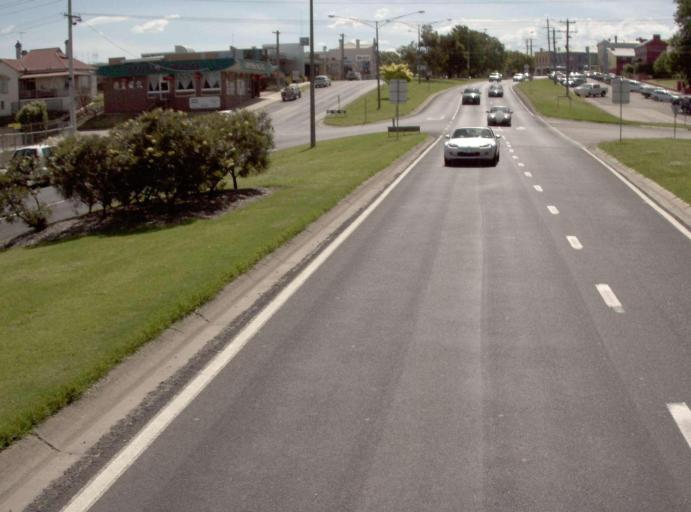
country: AU
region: Victoria
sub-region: East Gippsland
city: Bairnsdale
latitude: -37.8257
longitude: 147.6376
